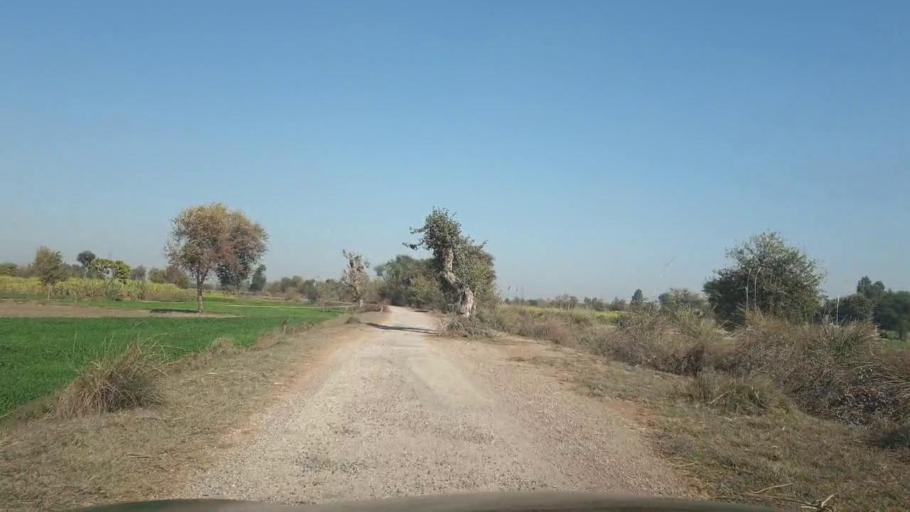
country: PK
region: Sindh
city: Ghotki
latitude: 27.9838
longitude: 69.4270
